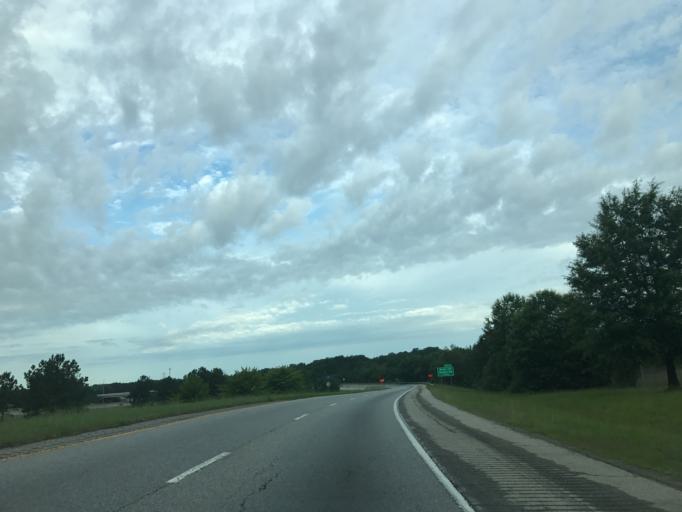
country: US
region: South Carolina
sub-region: Spartanburg County
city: Valley Falls
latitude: 35.0128
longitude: -81.9083
